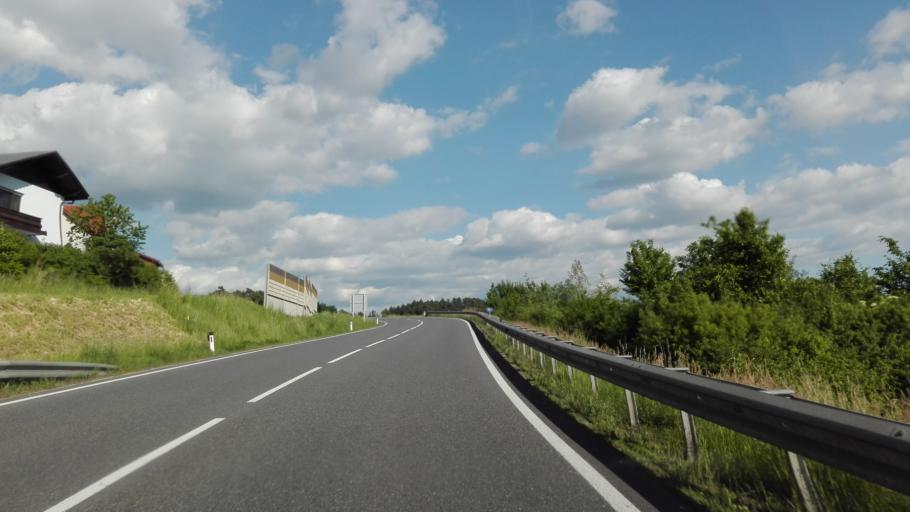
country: AT
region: Upper Austria
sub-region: Politischer Bezirk Perg
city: Perg
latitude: 48.3294
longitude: 14.6045
